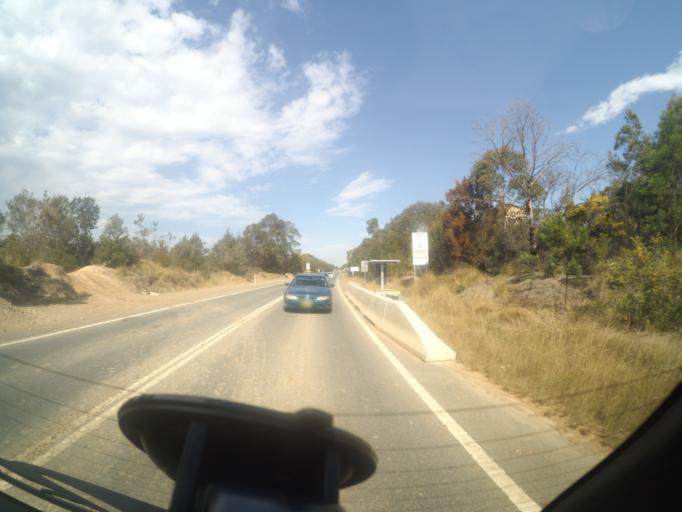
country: AU
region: New South Wales
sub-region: Liverpool
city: East Hills
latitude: -33.9937
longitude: 150.9968
